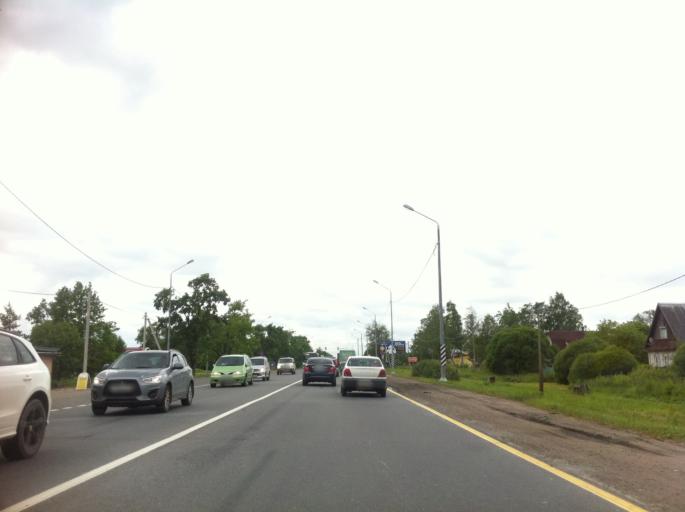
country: RU
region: Leningrad
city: Maloye Verevo
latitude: 59.6634
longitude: 30.2253
